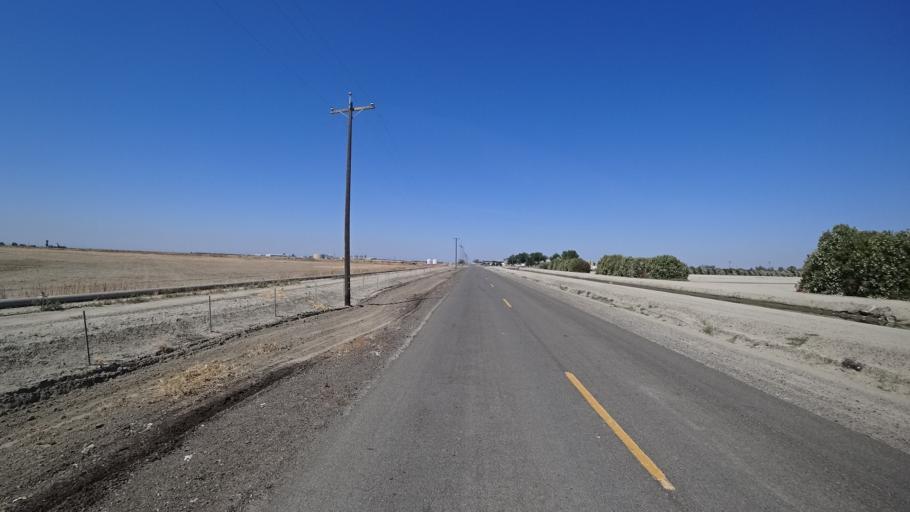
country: US
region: California
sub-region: Kings County
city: Corcoran
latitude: 36.0726
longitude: -119.5518
